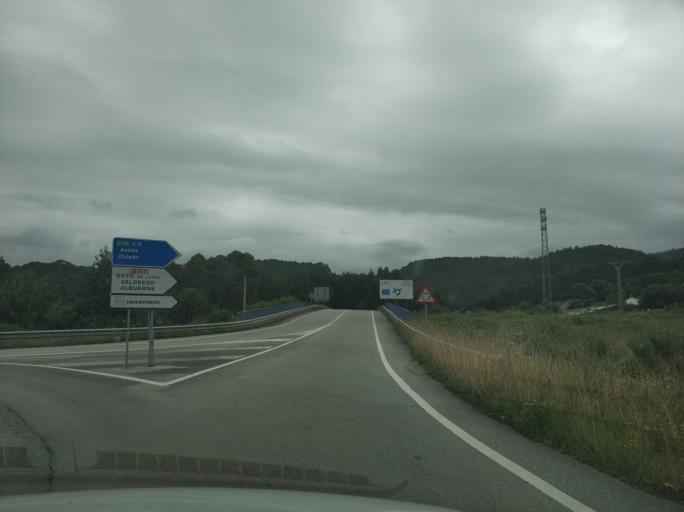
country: ES
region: Asturias
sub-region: Province of Asturias
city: Cudillero
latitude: 43.5658
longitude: -6.2415
